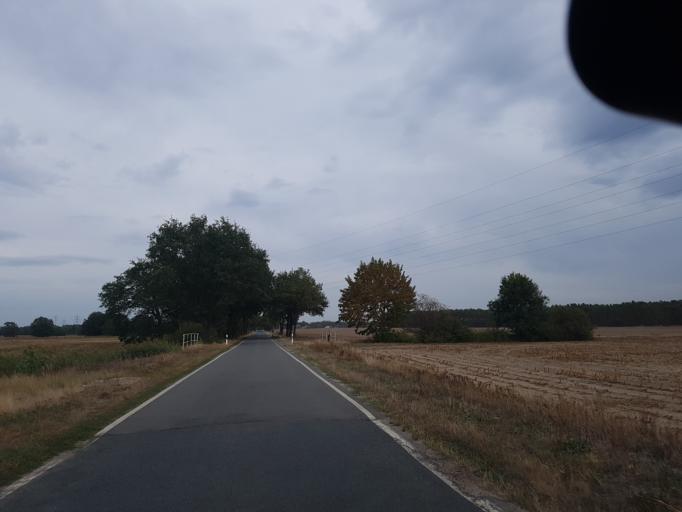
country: DE
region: Saxony-Anhalt
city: Annaburg
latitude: 51.7742
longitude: 13.0609
